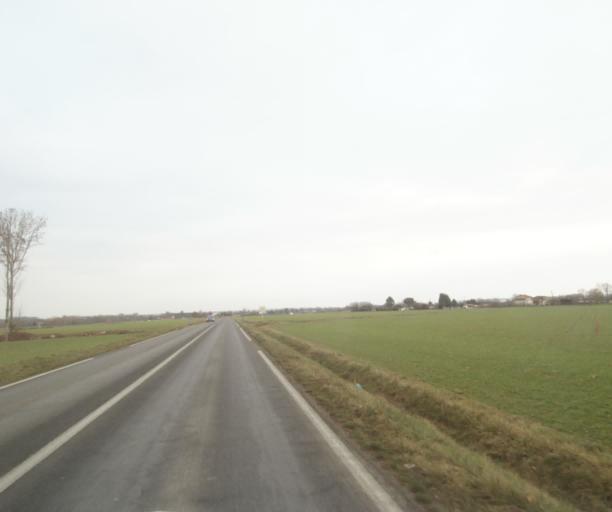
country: FR
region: Champagne-Ardenne
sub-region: Departement de la Haute-Marne
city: Saint-Dizier
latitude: 48.6216
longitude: 4.9285
